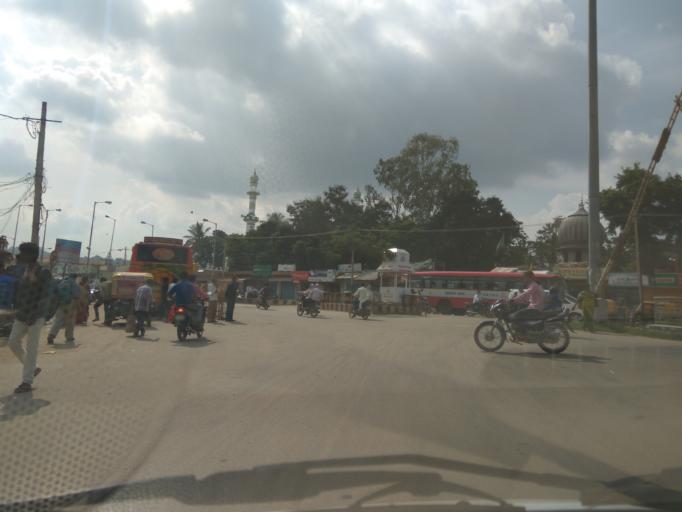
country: IN
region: Karnataka
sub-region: Kolar
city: Kolar
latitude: 13.1321
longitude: 78.1267
